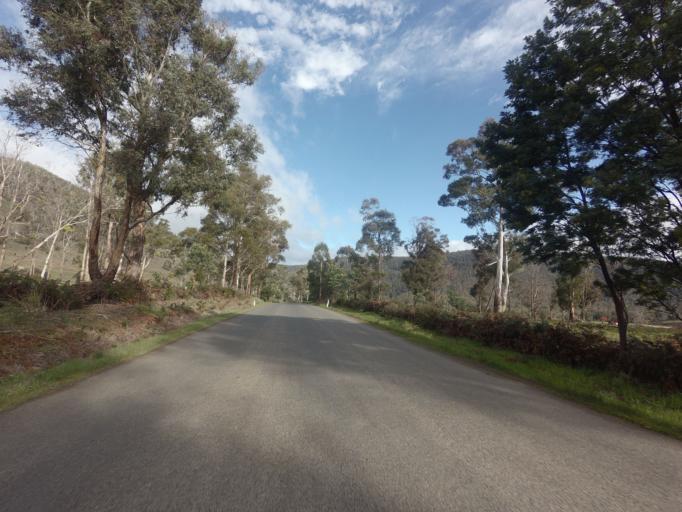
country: AU
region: Tasmania
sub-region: Derwent Valley
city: New Norfolk
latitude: -42.7771
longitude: 146.9659
